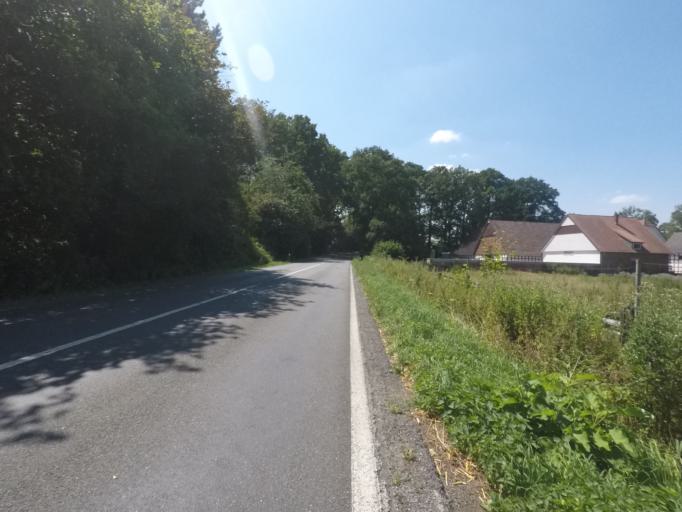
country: DE
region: North Rhine-Westphalia
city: Enger
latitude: 52.1071
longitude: 8.5952
